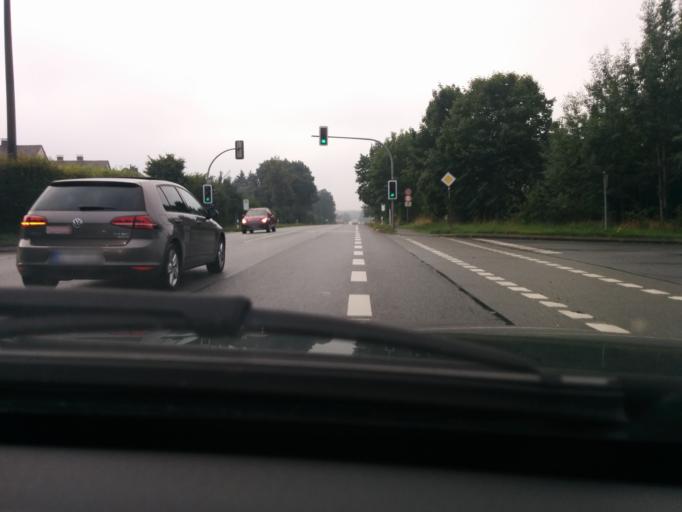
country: DE
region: North Rhine-Westphalia
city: Halle
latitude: 52.0386
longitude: 8.3919
